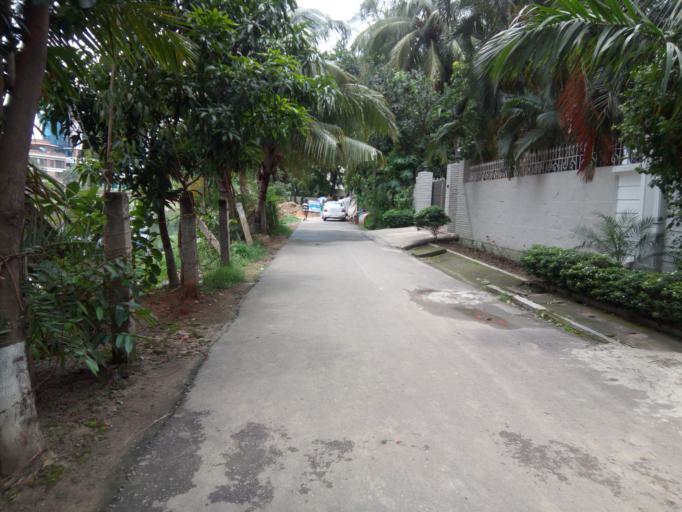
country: BD
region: Dhaka
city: Paltan
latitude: 23.7919
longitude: 90.4107
